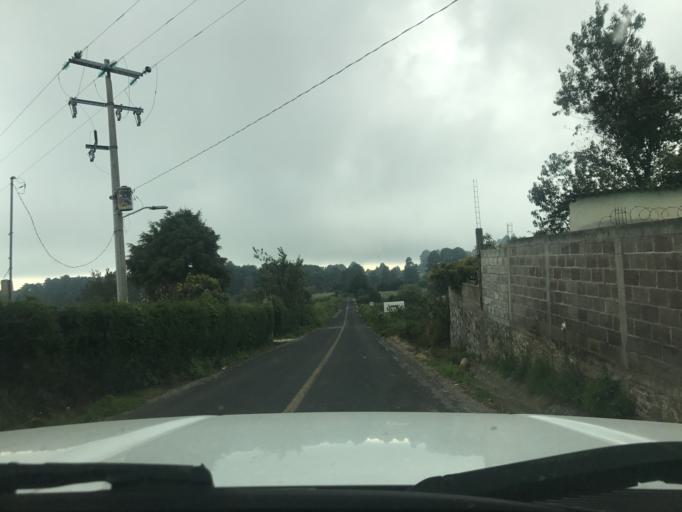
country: MX
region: Morelos
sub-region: Ocuituco
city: Huepalcalco (San Miguel)
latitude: 18.9153
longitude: -98.7464
